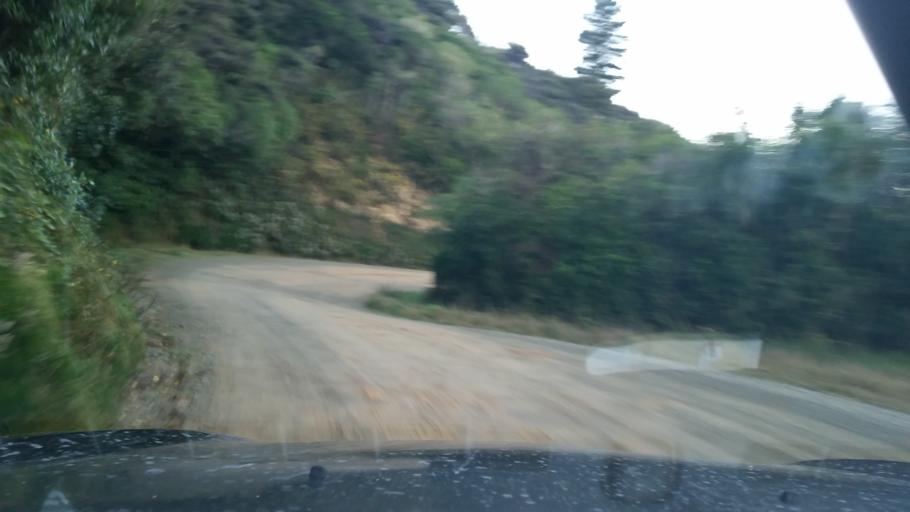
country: NZ
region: Marlborough
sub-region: Marlborough District
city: Picton
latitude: -41.1319
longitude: 174.1417
